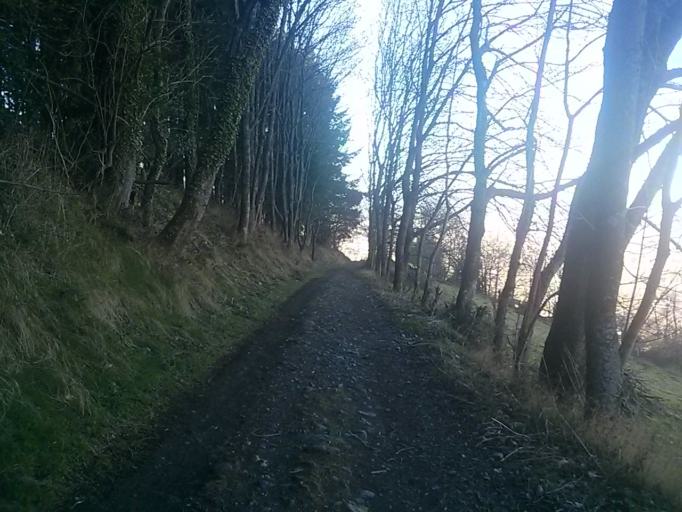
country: FR
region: Rhone-Alpes
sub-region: Departement de la Loire
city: Saint-Jean-Bonnefonds
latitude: 45.4167
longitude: 4.4387
